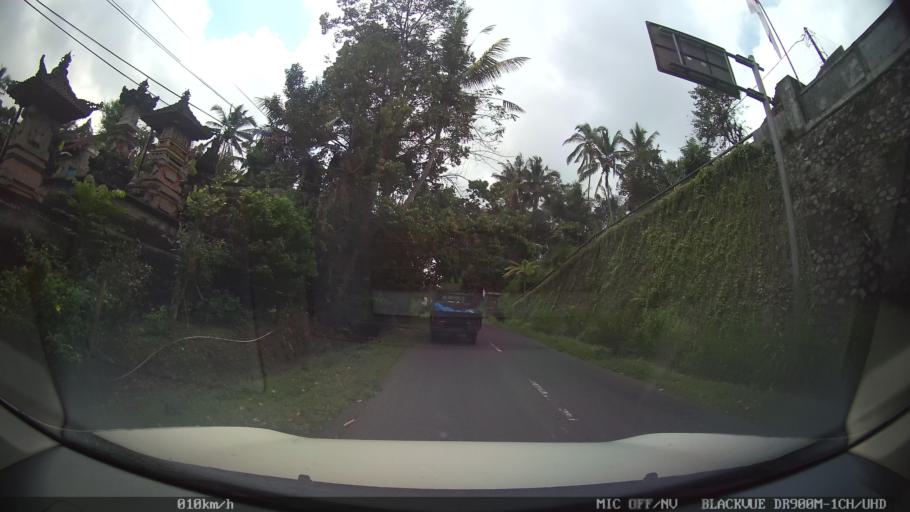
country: ID
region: Bali
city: Bangli
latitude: -8.4511
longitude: 115.3455
